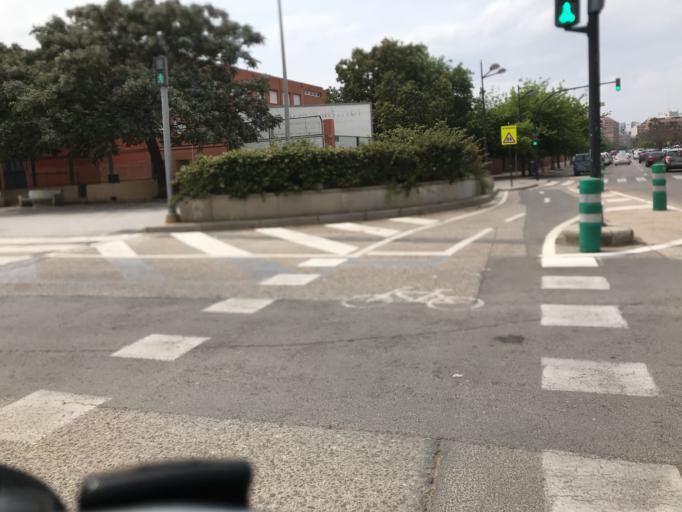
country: ES
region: Valencia
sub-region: Provincia de Valencia
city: Valencia
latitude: 39.4591
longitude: -0.3403
